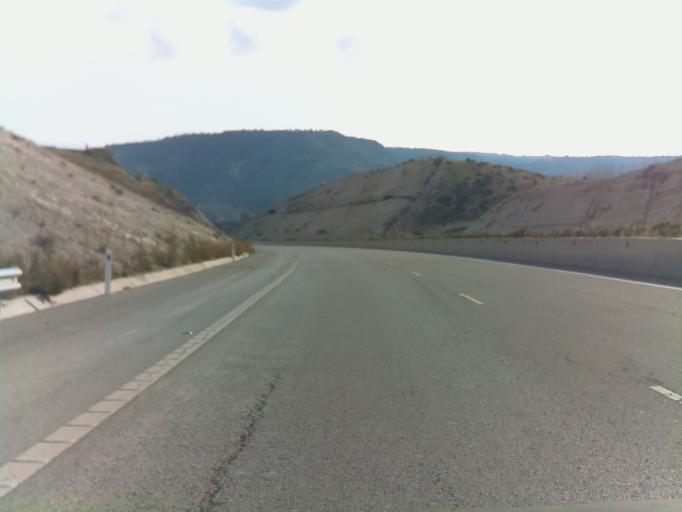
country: CY
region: Limassol
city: Pissouri
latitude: 34.6673
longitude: 32.6456
